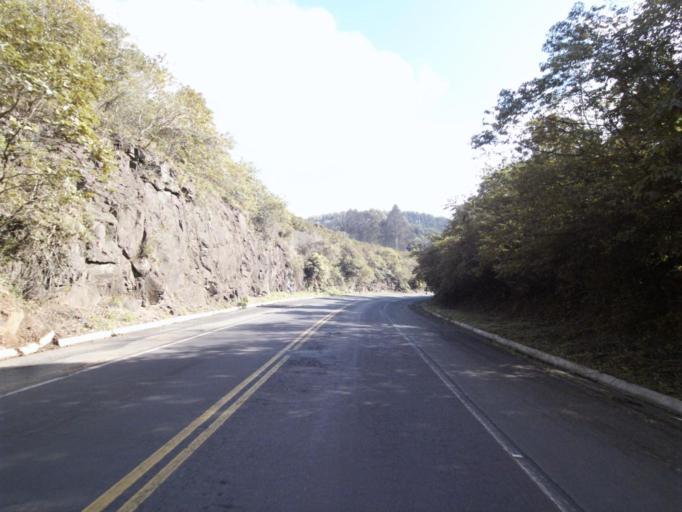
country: BR
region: Rio Grande do Sul
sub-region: Frederico Westphalen
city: Frederico Westphalen
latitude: -27.1425
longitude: -53.2143
